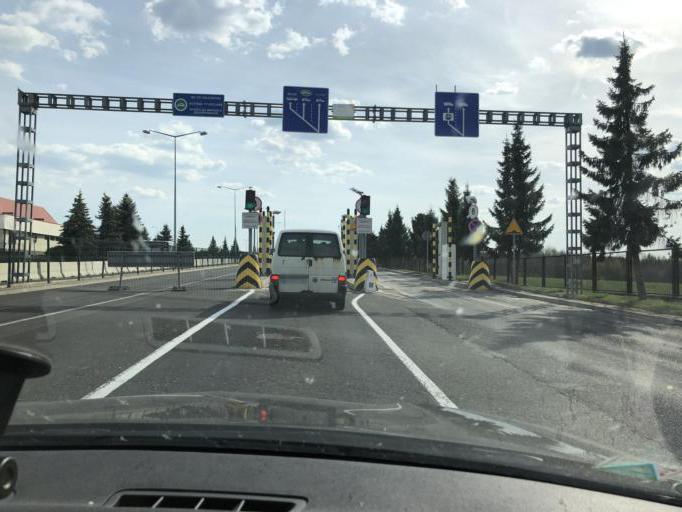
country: PL
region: Subcarpathian Voivodeship
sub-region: Powiat lubaczowski
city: Wielkie Oczy
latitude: 49.9569
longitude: 23.1093
